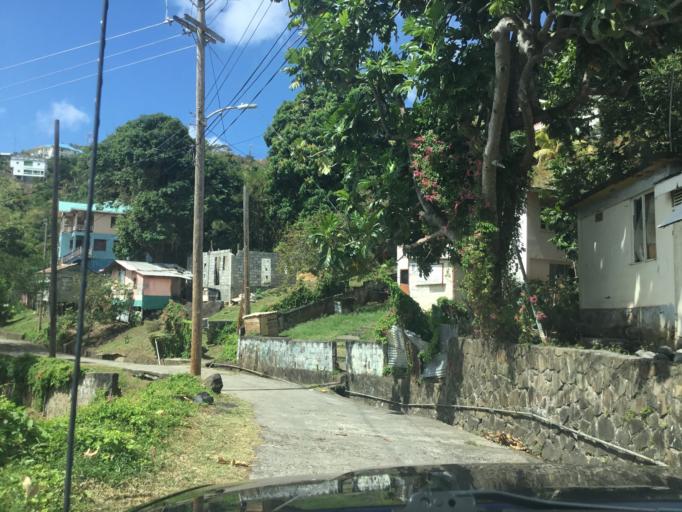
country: VC
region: Saint George
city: Kingstown Park
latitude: 13.1599
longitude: -61.2356
